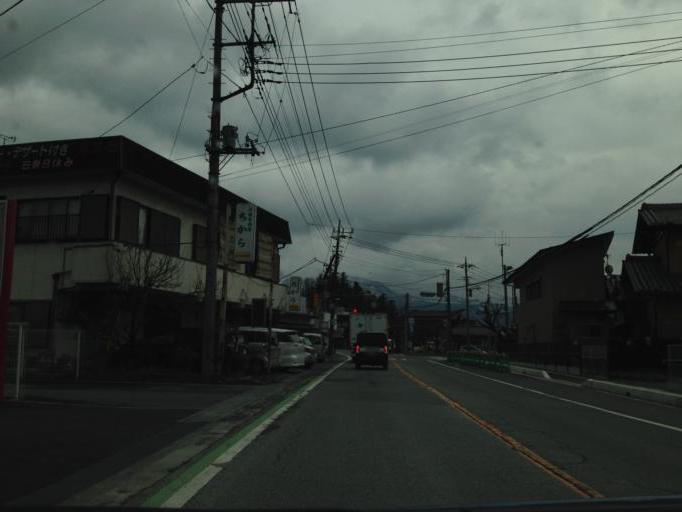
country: JP
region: Saitama
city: Chichibu
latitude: 36.0140
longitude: 139.0866
